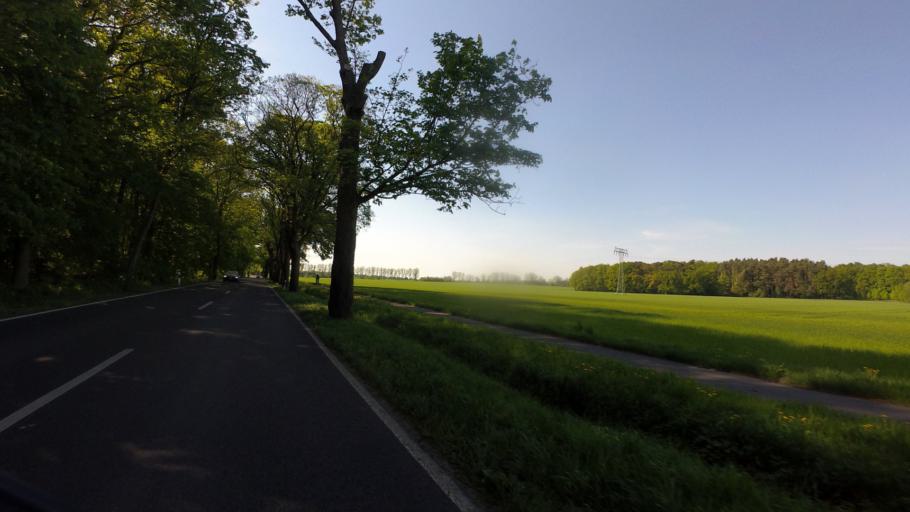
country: DE
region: Brandenburg
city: Grossbeeren
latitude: 52.3468
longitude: 13.3378
